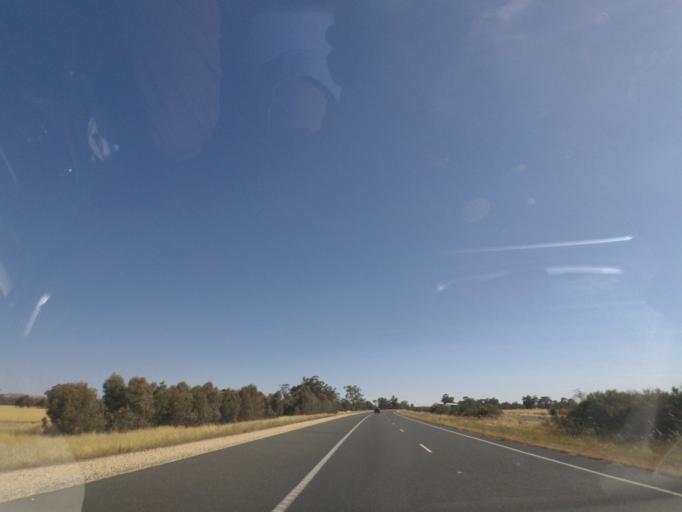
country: AU
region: Victoria
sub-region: Greater Shepparton
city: Shepparton
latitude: -36.8045
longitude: 145.1774
